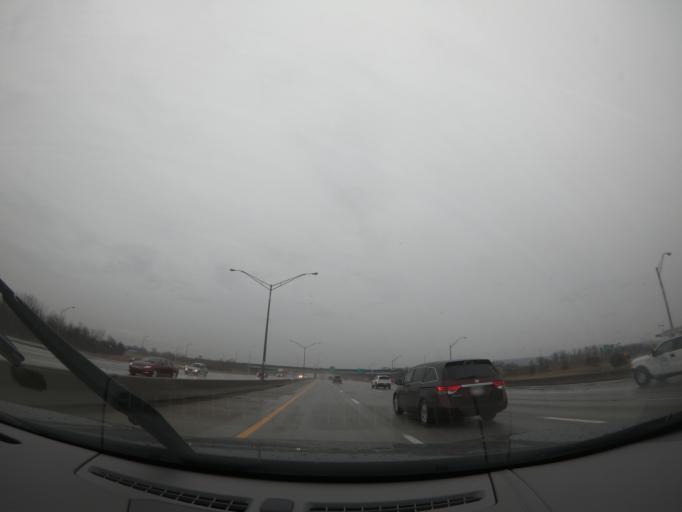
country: US
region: Kentucky
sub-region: Jefferson County
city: Heritage Creek
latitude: 38.1392
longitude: -85.7082
